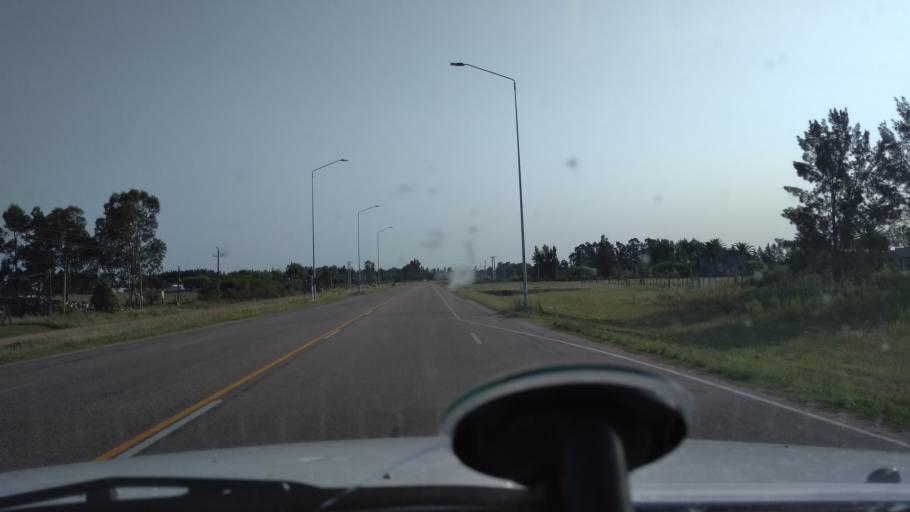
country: UY
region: Canelones
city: Sauce
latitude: -34.6497
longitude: -56.0503
